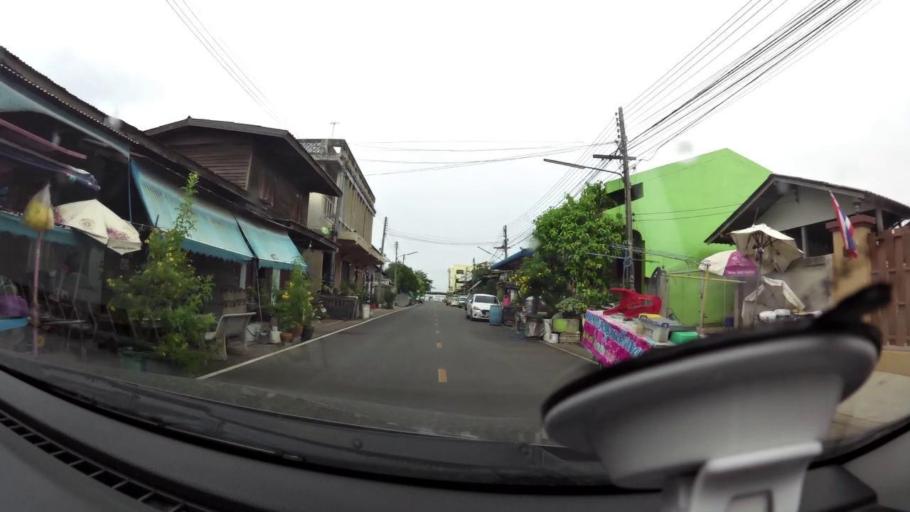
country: TH
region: Prachuap Khiri Khan
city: Pran Buri
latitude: 12.4021
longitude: 99.9927
